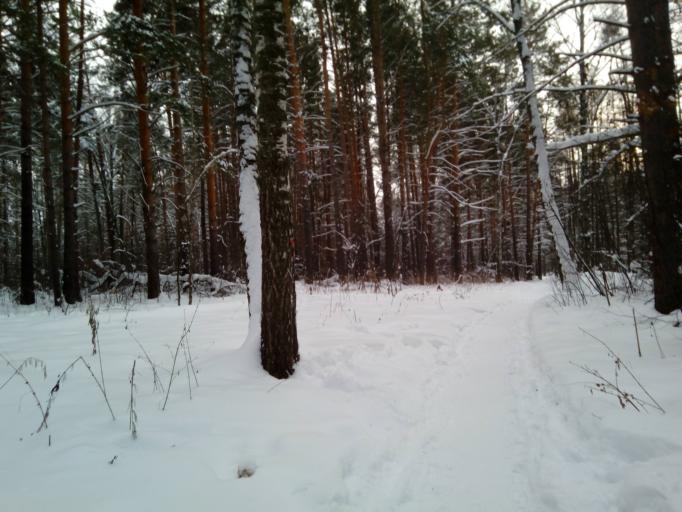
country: RU
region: Novosibirsk
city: Akademgorodok
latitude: 54.8577
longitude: 83.0928
